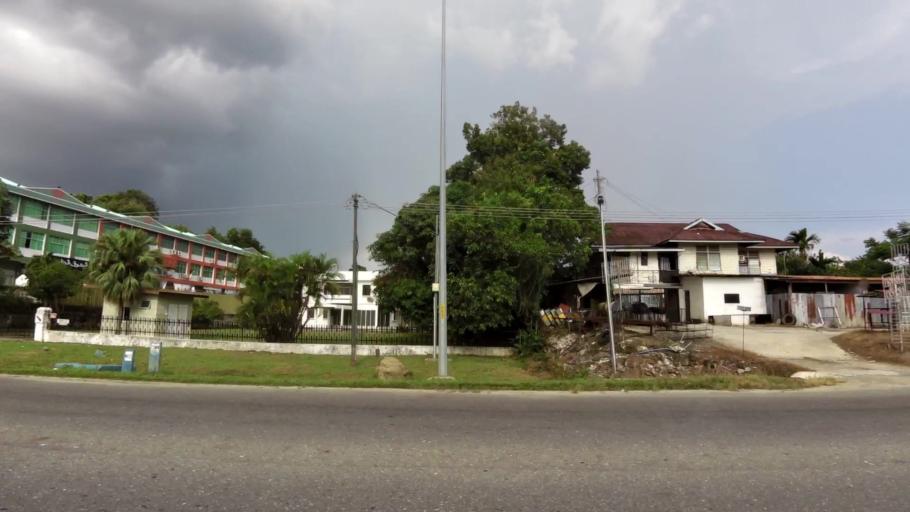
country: BN
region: Brunei and Muara
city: Bandar Seri Begawan
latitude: 4.9596
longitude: 114.9744
